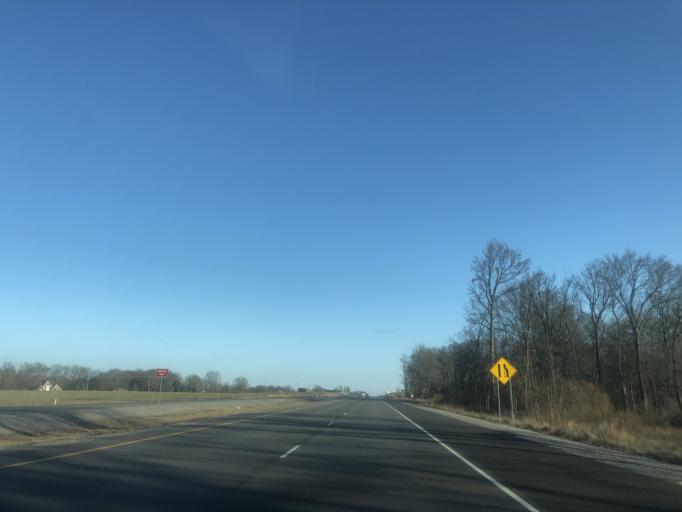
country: US
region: Tennessee
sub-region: Sumner County
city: Portland
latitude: 36.6249
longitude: -86.5622
